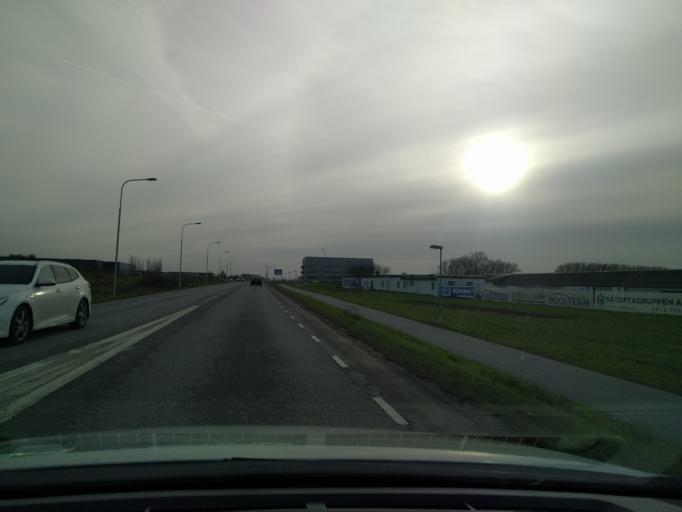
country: SE
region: Skane
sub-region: Malmo
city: Bunkeflostrand
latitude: 55.5579
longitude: 12.9836
